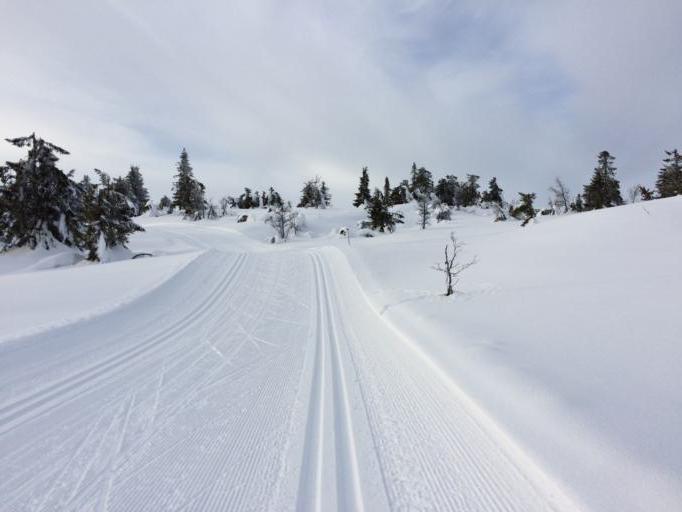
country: NO
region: Oppland
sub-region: Gausdal
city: Segalstad bru
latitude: 61.3264
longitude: 10.0383
